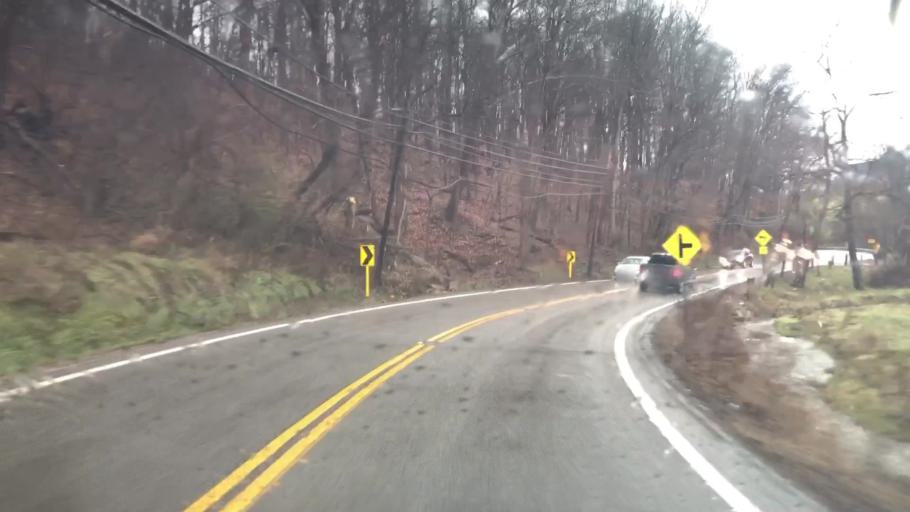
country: US
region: Ohio
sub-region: Belmont County
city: Saint Clairsville
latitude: 40.0907
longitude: -80.9094
